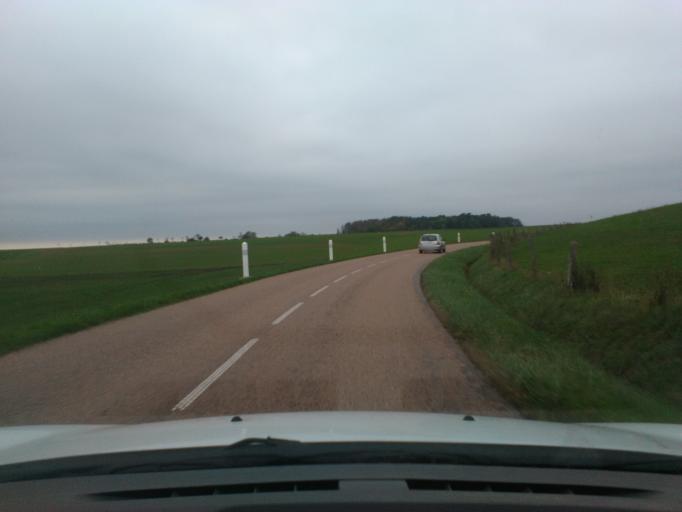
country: FR
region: Lorraine
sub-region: Departement des Vosges
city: Charmes
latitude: 48.3013
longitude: 6.2530
